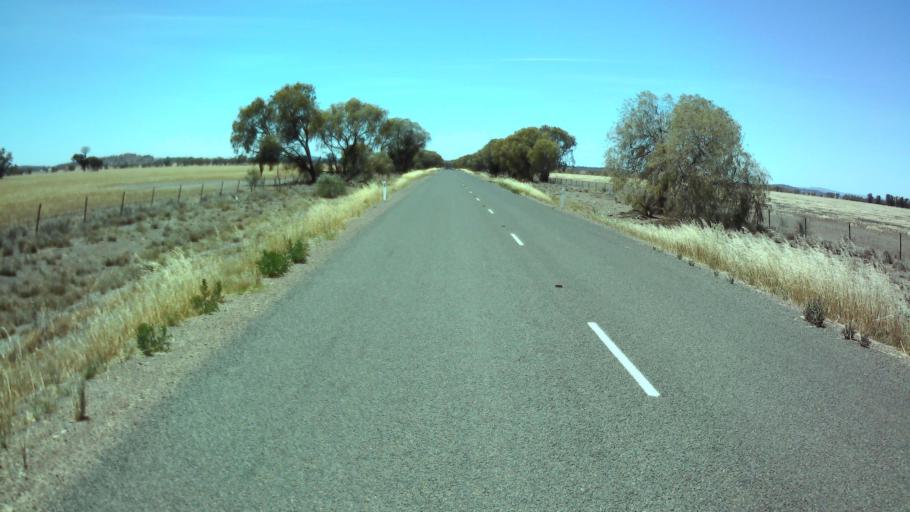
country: AU
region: New South Wales
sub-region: Bland
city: West Wyalong
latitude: -33.6613
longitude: 147.6088
